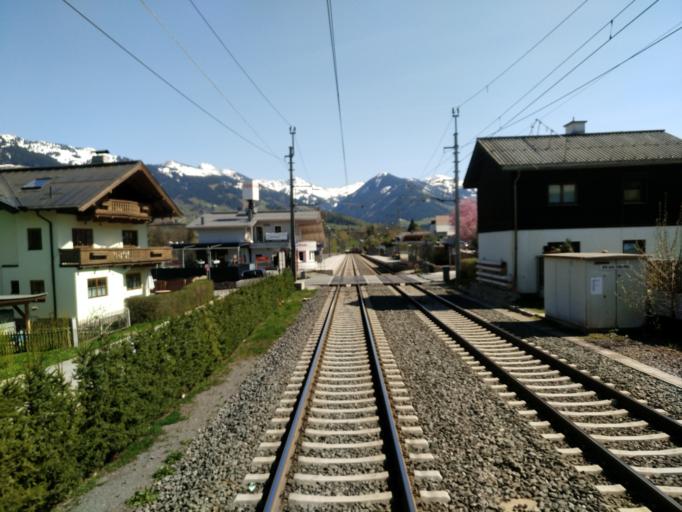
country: AT
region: Tyrol
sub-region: Politischer Bezirk Kitzbuhel
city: Kitzbuhel
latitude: 47.4439
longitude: 12.3887
